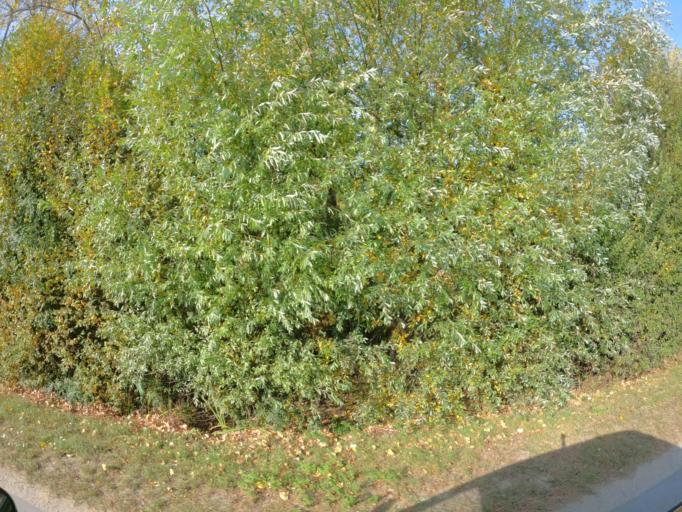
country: FR
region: Pays de la Loire
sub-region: Departement de la Vendee
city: Le Perrier
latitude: 46.8148
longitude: -1.9907
